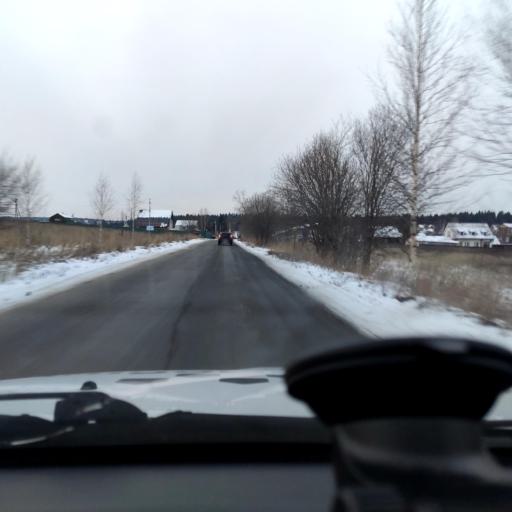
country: RU
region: Perm
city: Ferma
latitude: 57.9333
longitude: 56.3268
